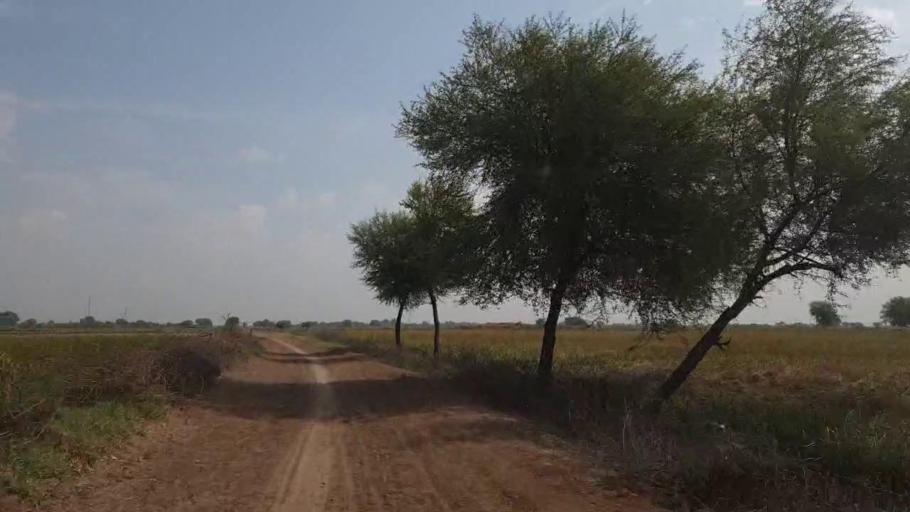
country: PK
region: Sindh
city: Rajo Khanani
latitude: 24.9542
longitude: 69.0229
